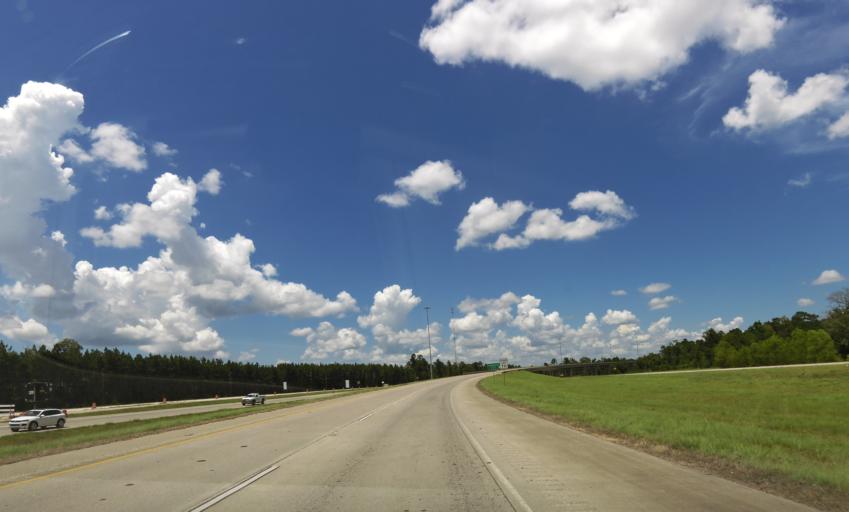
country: US
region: Texas
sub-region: San Jacinto County
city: Shepherd
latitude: 30.4682
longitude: -95.0170
